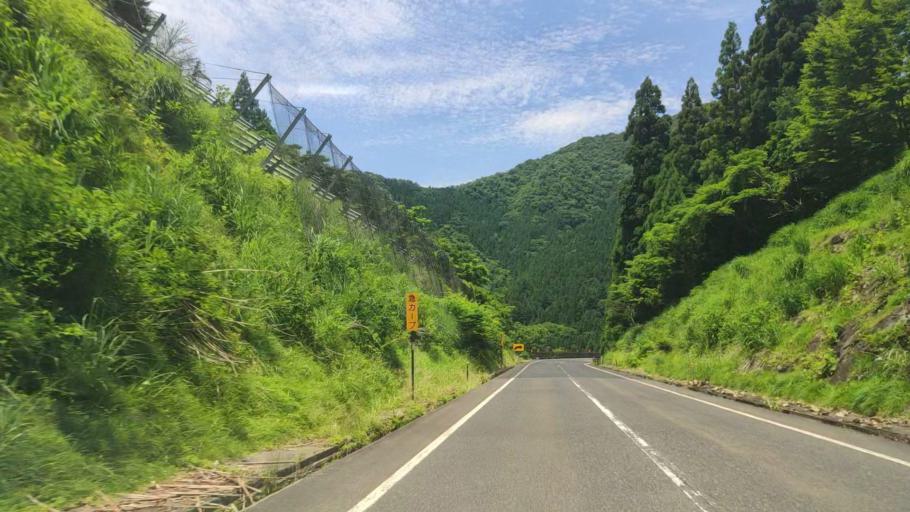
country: JP
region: Tottori
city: Tottori
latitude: 35.3452
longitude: 134.4524
